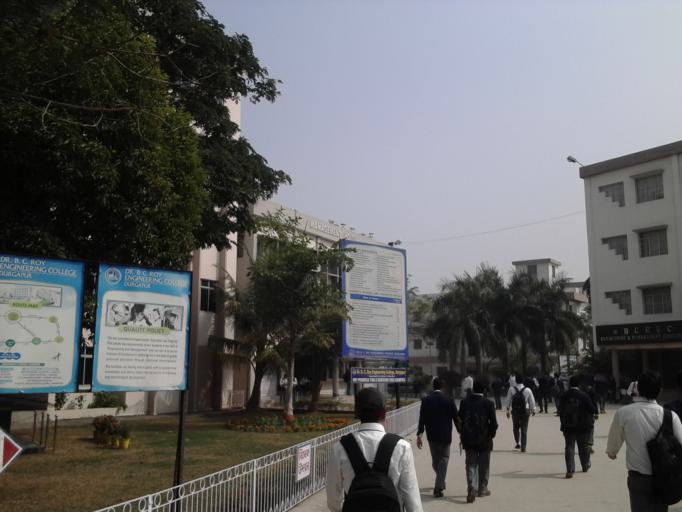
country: IN
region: West Bengal
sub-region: Barddhaman
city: Durgapur
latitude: 23.5447
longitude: 87.3420
